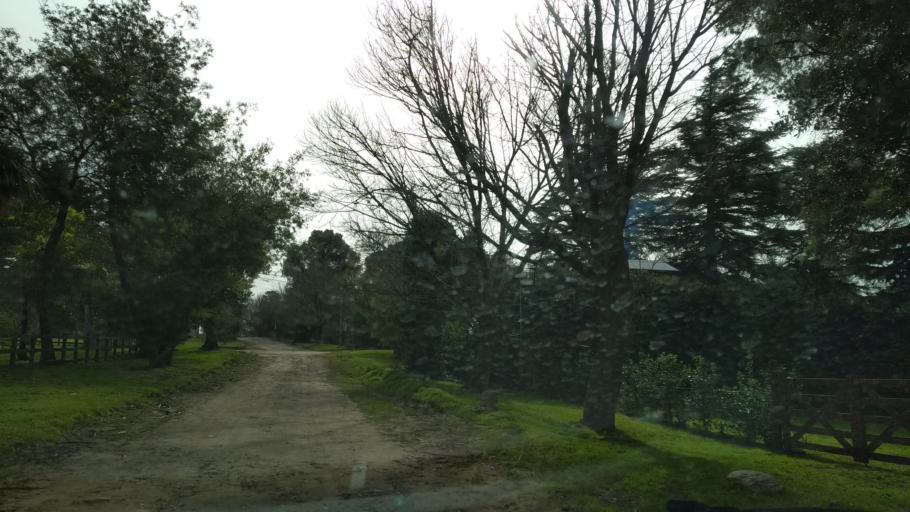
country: AR
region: Buenos Aires
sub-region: Partido de Tornquist
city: Tornquist
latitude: -38.0859
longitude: -61.9299
